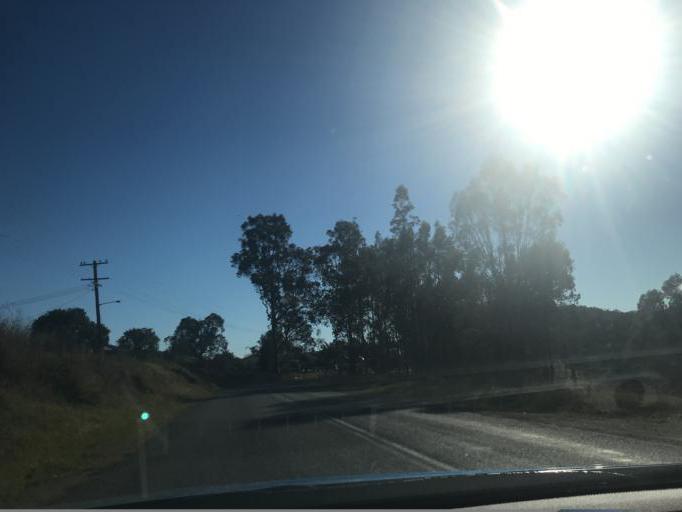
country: AU
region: New South Wales
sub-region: Cessnock
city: Cessnock
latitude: -32.9065
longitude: 151.2851
